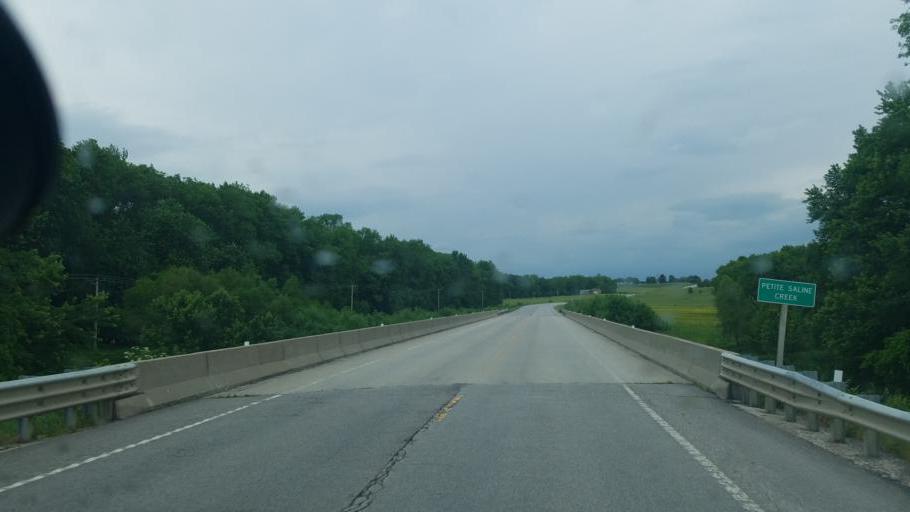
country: US
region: Missouri
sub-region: Cooper County
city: Boonville
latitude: 38.9184
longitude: -92.6862
